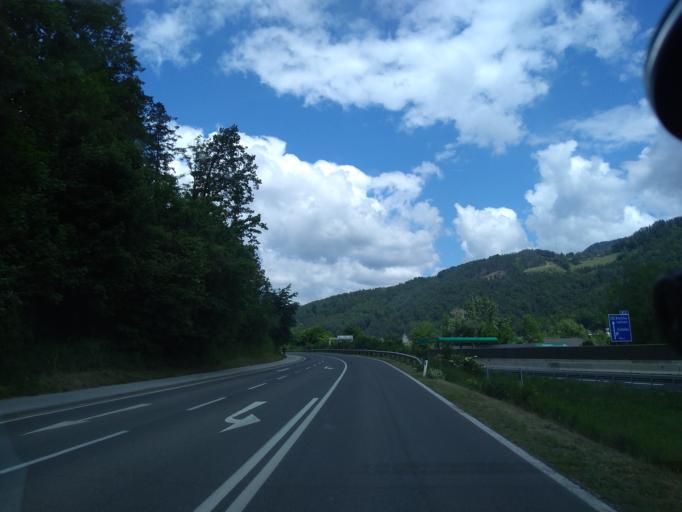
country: AT
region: Styria
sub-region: Politischer Bezirk Graz-Umgebung
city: Frohnleiten
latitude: 47.2742
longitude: 15.3273
